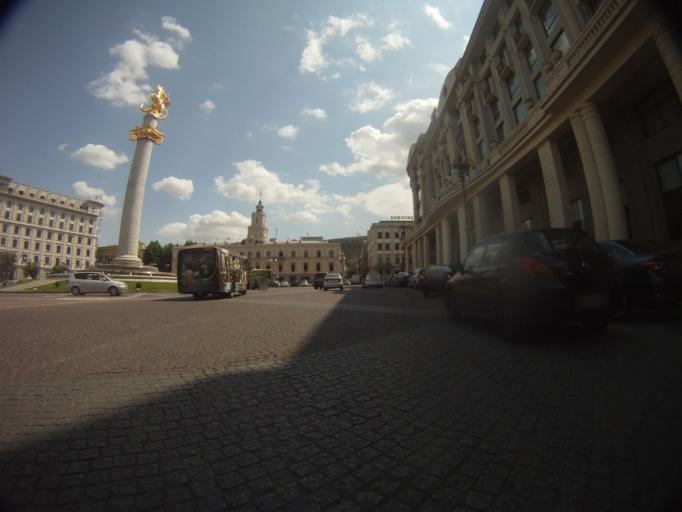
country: GE
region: T'bilisi
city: Tbilisi
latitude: 41.6949
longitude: 44.8003
